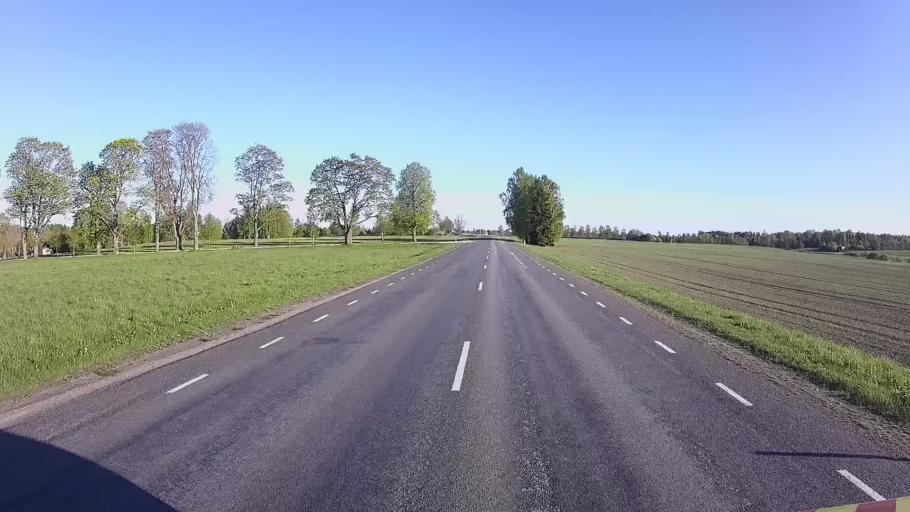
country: EE
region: Viljandimaa
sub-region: Viljandi linn
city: Viljandi
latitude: 58.3956
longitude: 25.5922
